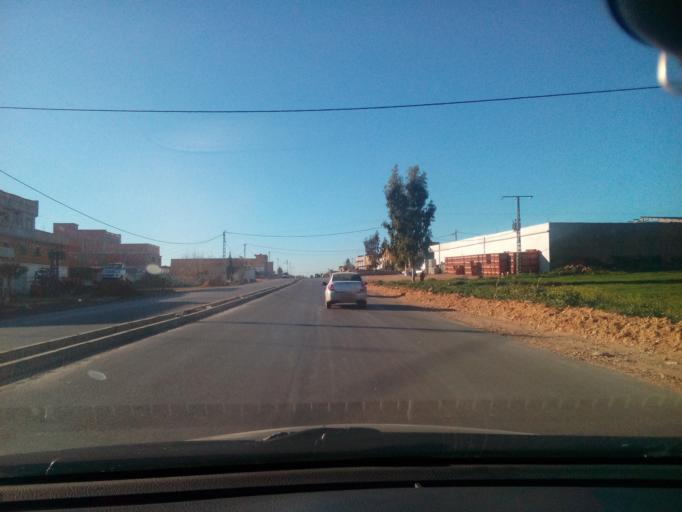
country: DZ
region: Mostaganem
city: Mostaganem
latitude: 35.9094
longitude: 0.1629
